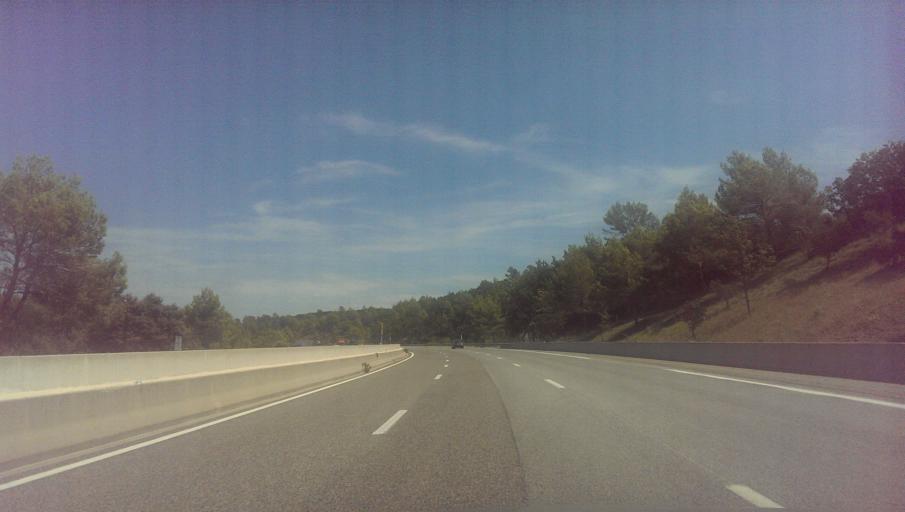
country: FR
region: Provence-Alpes-Cote d'Azur
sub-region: Departement du Var
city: Cabasse
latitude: 43.3998
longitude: 6.2237
